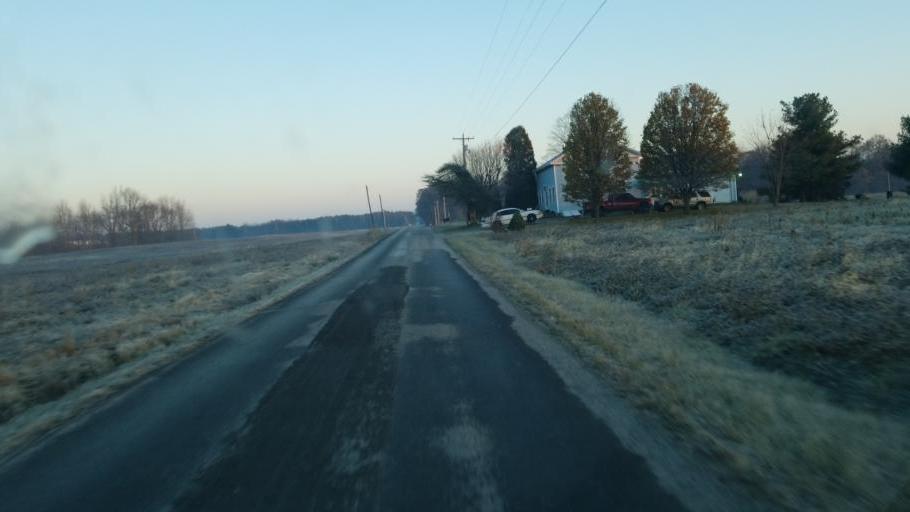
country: US
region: Ohio
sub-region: Wayne County
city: West Salem
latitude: 40.9713
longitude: -82.0780
